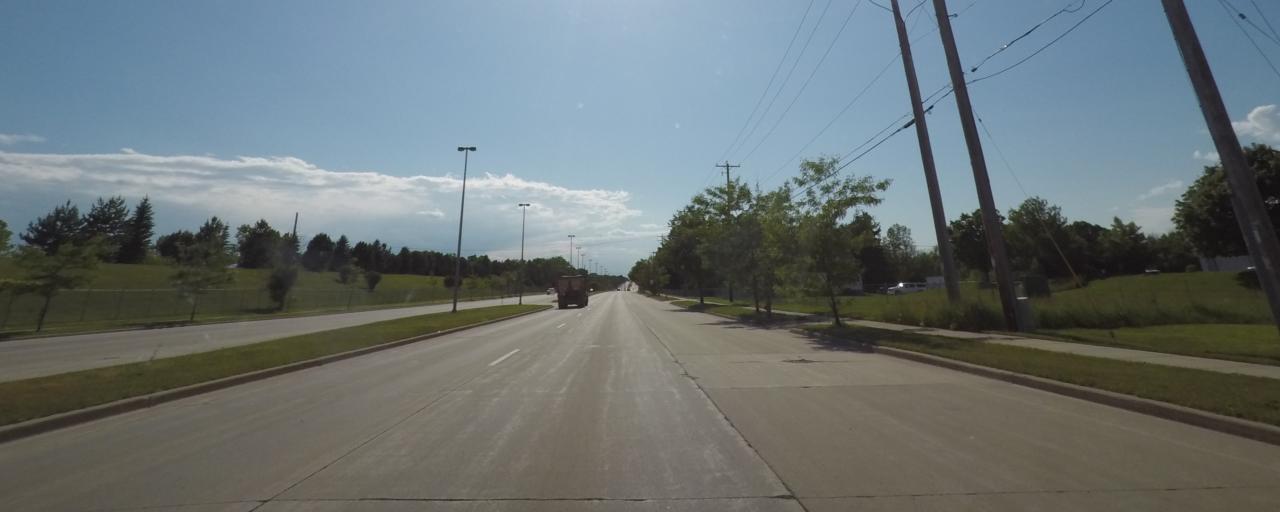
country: US
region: Wisconsin
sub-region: Milwaukee County
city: Greendale
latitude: 42.9160
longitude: -87.9866
